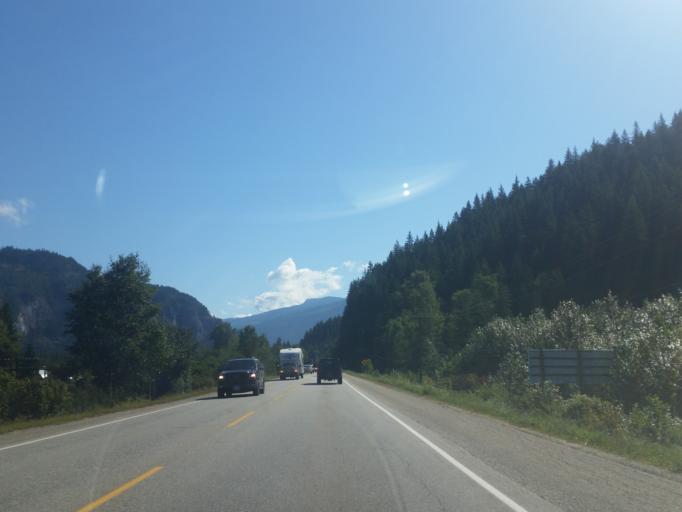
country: CA
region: British Columbia
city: Sicamous
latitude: 50.8859
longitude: -118.8962
